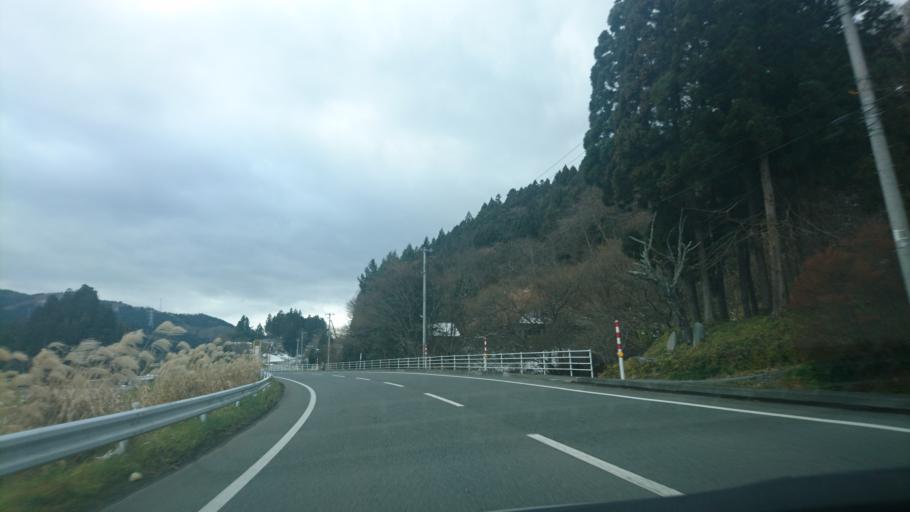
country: JP
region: Iwate
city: Mizusawa
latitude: 39.1822
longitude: 141.2911
